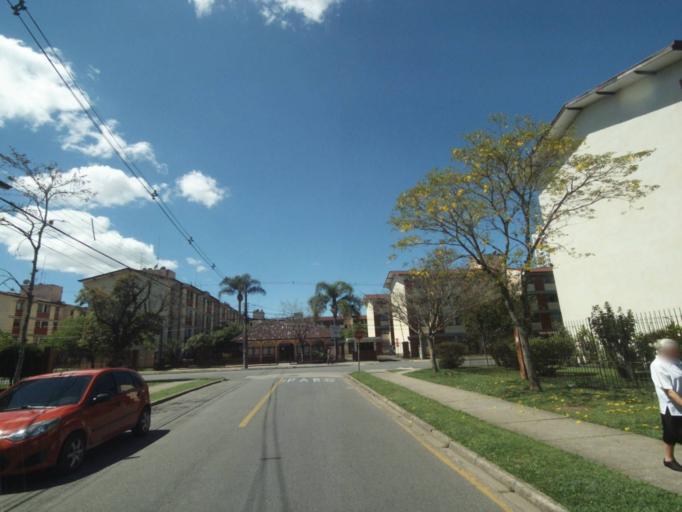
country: BR
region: Parana
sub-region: Curitiba
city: Curitiba
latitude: -25.3880
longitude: -49.2383
